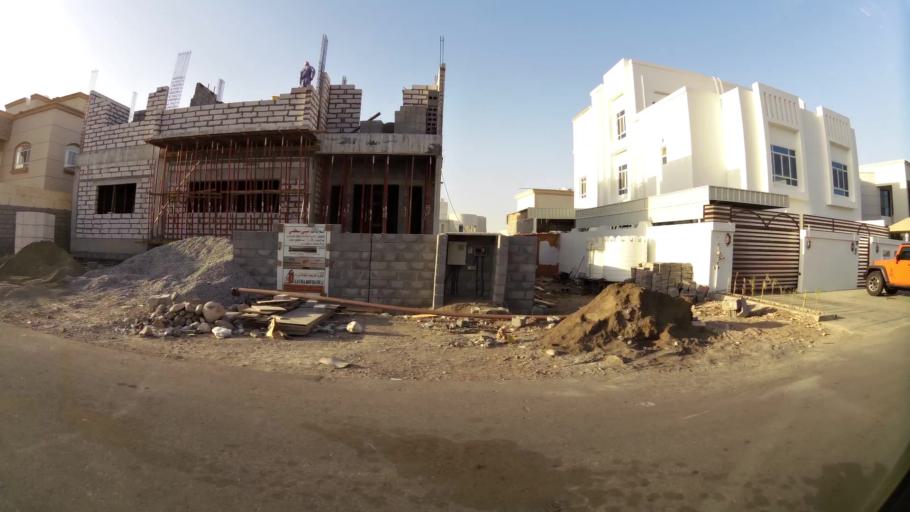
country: OM
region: Muhafazat Masqat
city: As Sib al Jadidah
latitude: 23.5900
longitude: 58.1386
